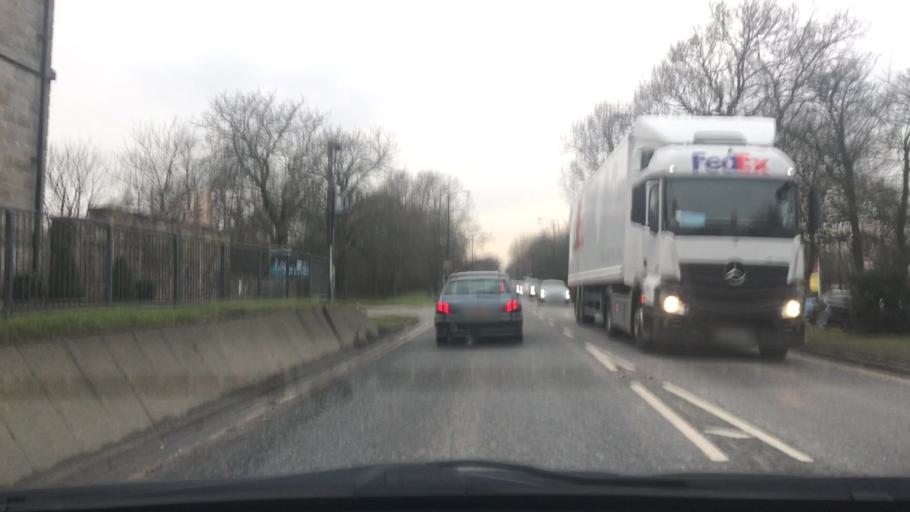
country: GB
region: England
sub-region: North Yorkshire
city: Knaresborough
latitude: 53.9844
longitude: -1.4925
